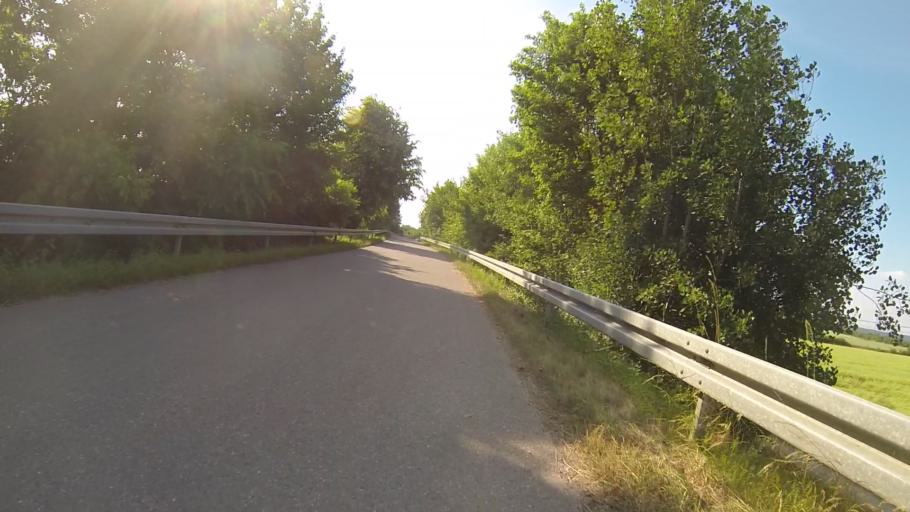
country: DE
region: Bavaria
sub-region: Swabia
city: Neu-Ulm
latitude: 48.3998
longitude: 10.0477
